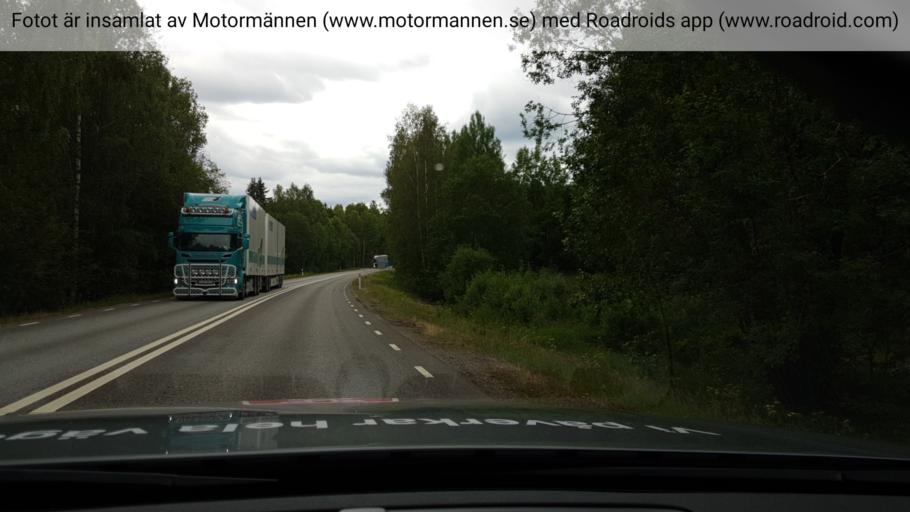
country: SE
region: Vaestmanland
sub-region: Skinnskattebergs Kommun
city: Skinnskatteberg
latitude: 59.8433
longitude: 15.6805
